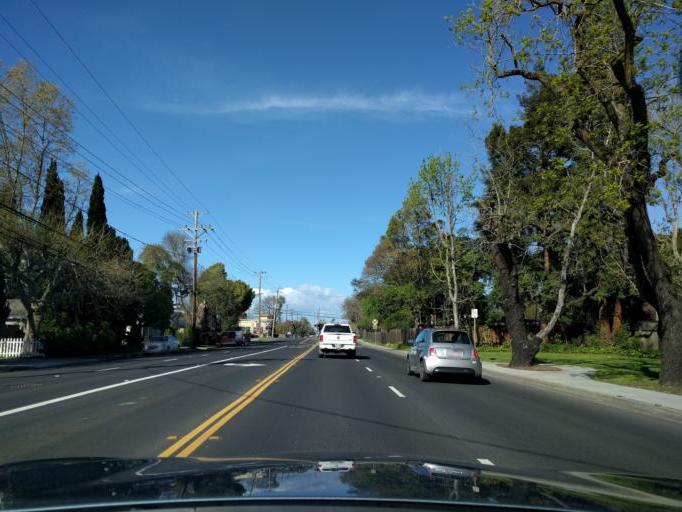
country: US
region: California
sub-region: San Mateo County
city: North Fair Oaks
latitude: 37.4770
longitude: -122.1866
